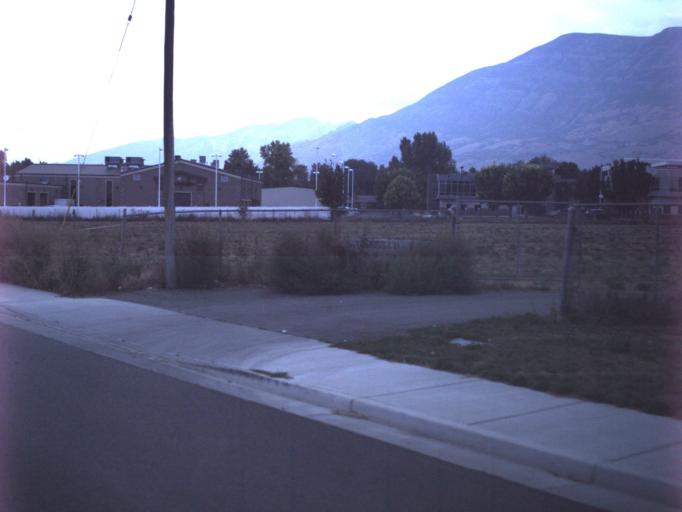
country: US
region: Utah
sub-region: Utah County
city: Lindon
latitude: 40.3478
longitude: -111.7266
